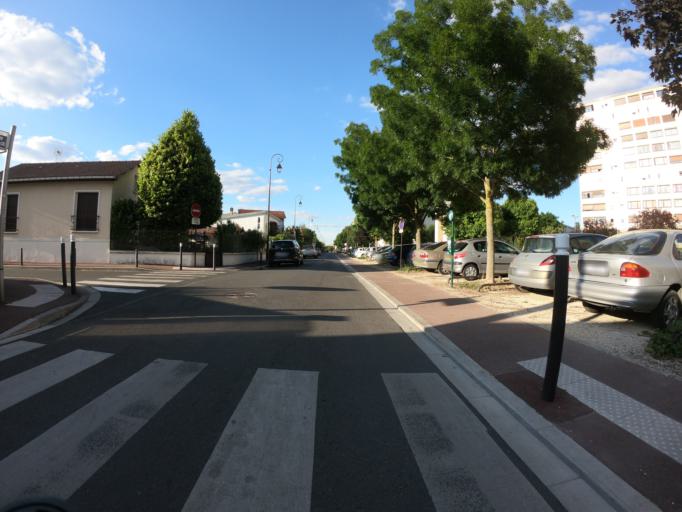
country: FR
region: Ile-de-France
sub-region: Departement du Val-de-Marne
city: Fresnes
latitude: 48.7577
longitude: 2.3109
